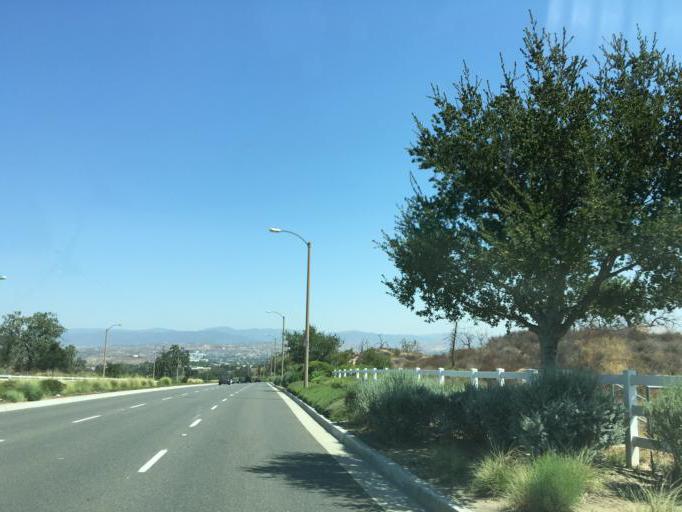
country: US
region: California
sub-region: Los Angeles County
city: Santa Clarita
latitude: 34.3954
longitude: -118.5749
